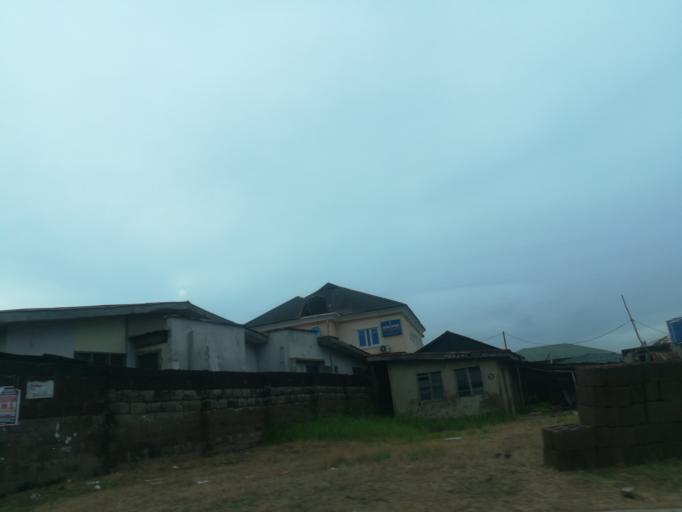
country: NG
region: Oyo
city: Egbeda
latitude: 7.4056
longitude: 3.9792
